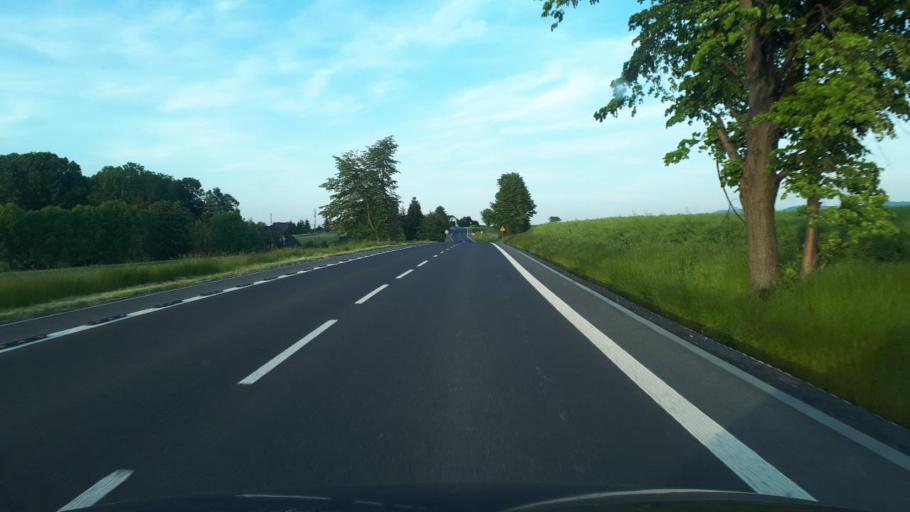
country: PL
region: Silesian Voivodeship
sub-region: Powiat bielski
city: Mazancowice
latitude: 49.8547
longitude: 18.9576
